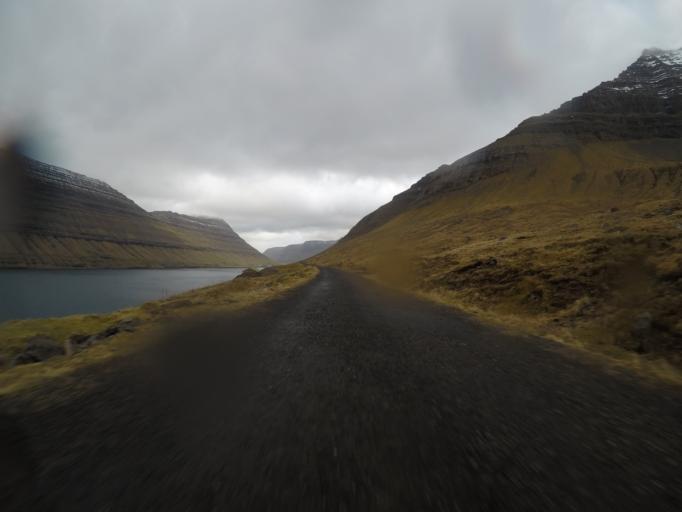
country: FO
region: Nordoyar
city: Klaksvik
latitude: 62.3185
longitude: -6.5576
